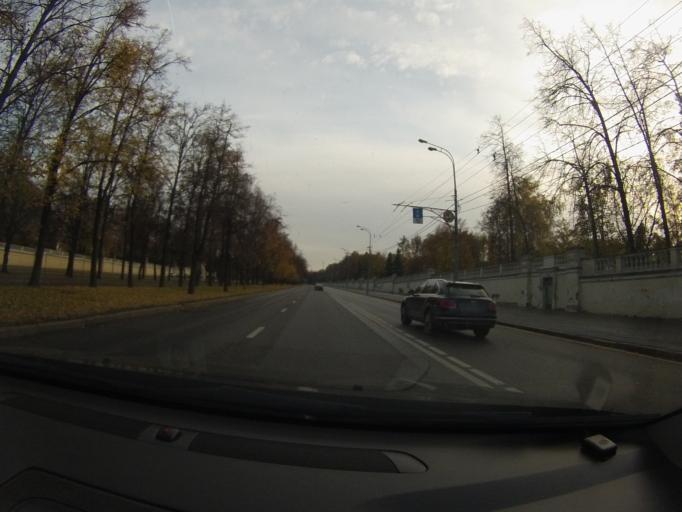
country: RU
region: Moscow
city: Vorob'yovo
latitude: 55.7205
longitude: 37.5348
